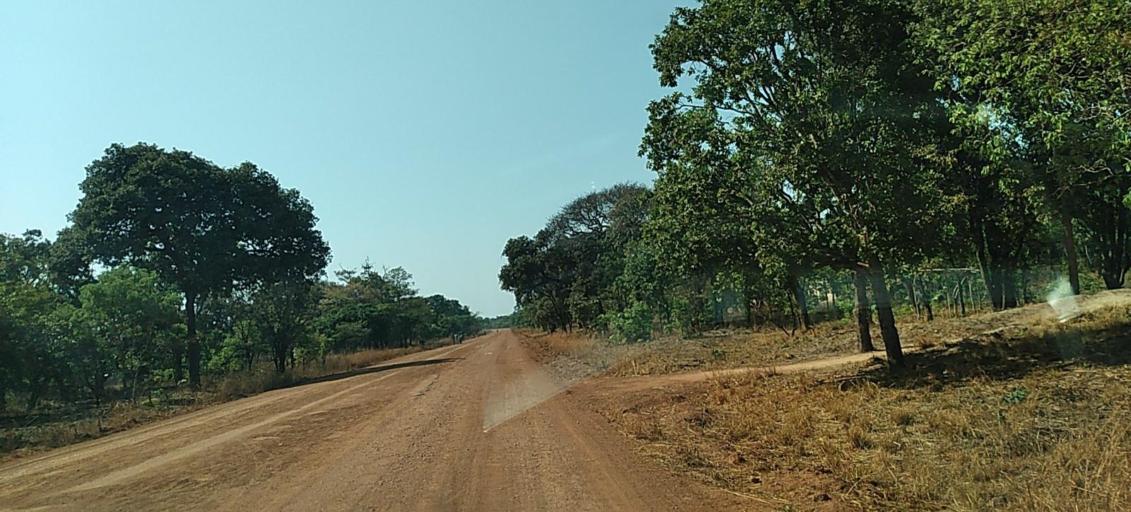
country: ZM
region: North-Western
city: Mwinilunga
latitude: -11.9256
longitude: 25.3205
